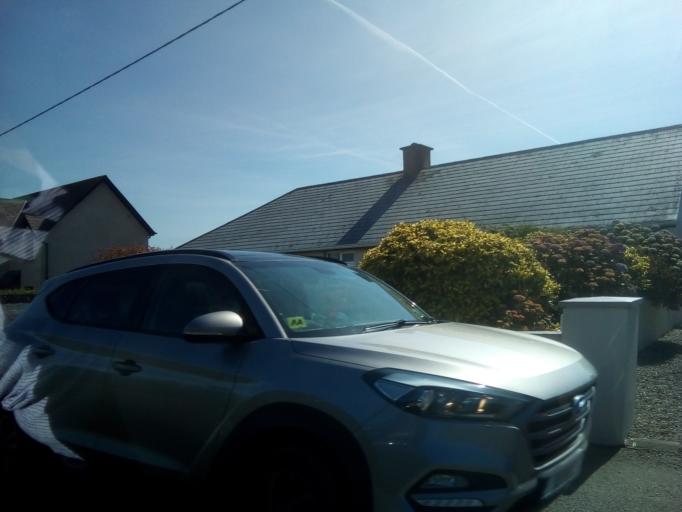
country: IE
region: Leinster
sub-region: Loch Garman
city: Loch Garman
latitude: 52.1792
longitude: -6.5837
